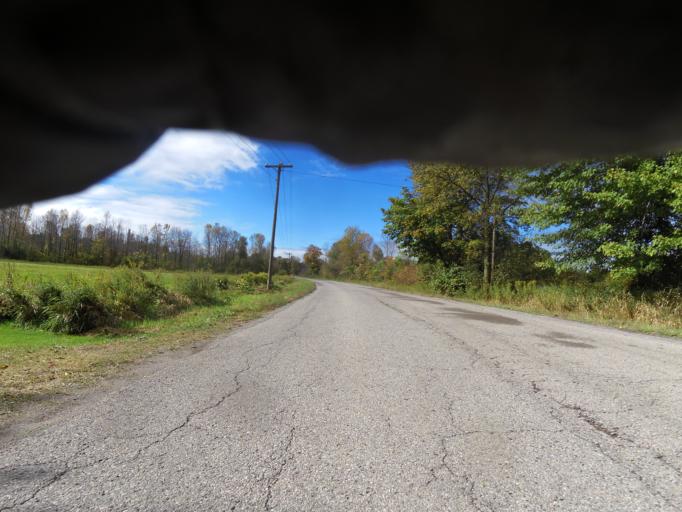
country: CA
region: Ontario
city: Cobourg
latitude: 43.9365
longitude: -78.3720
